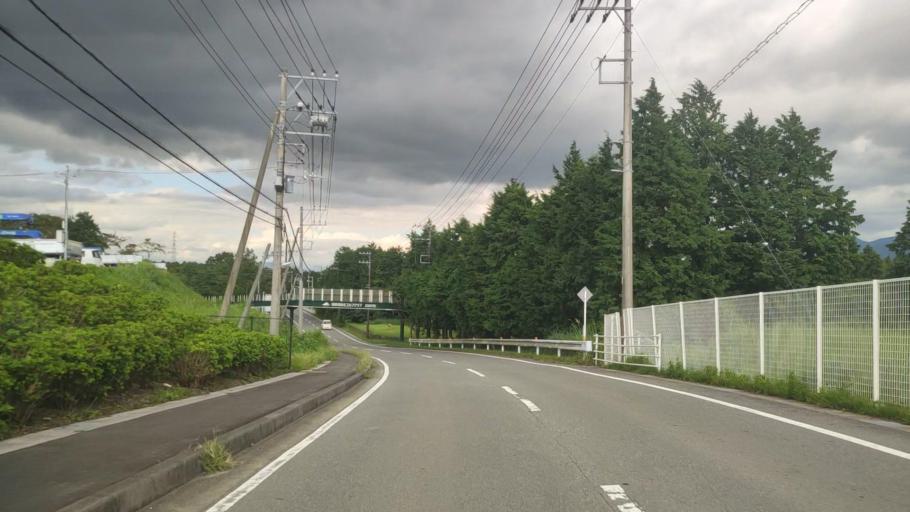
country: JP
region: Shizuoka
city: Gotemba
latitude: 35.2712
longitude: 138.8961
